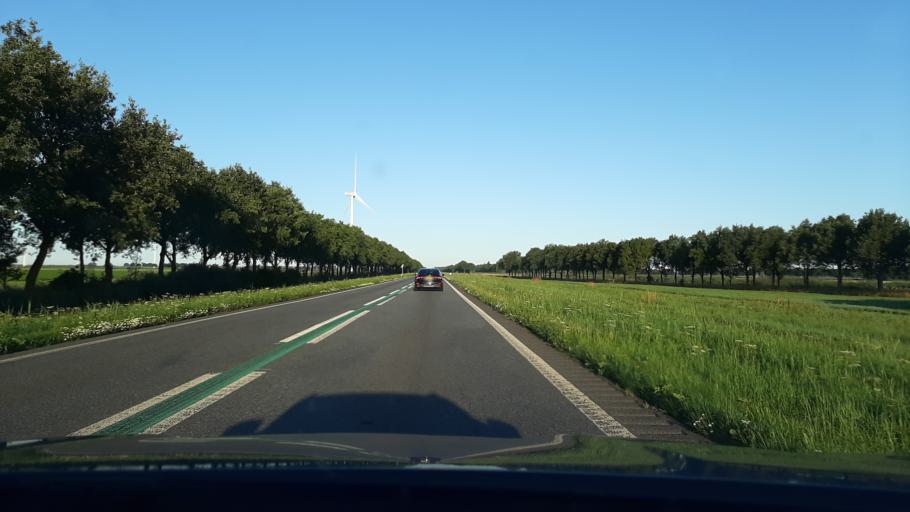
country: NL
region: Utrecht
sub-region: Gemeente Bunschoten
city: Spakenburg
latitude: 52.3162
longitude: 5.3937
